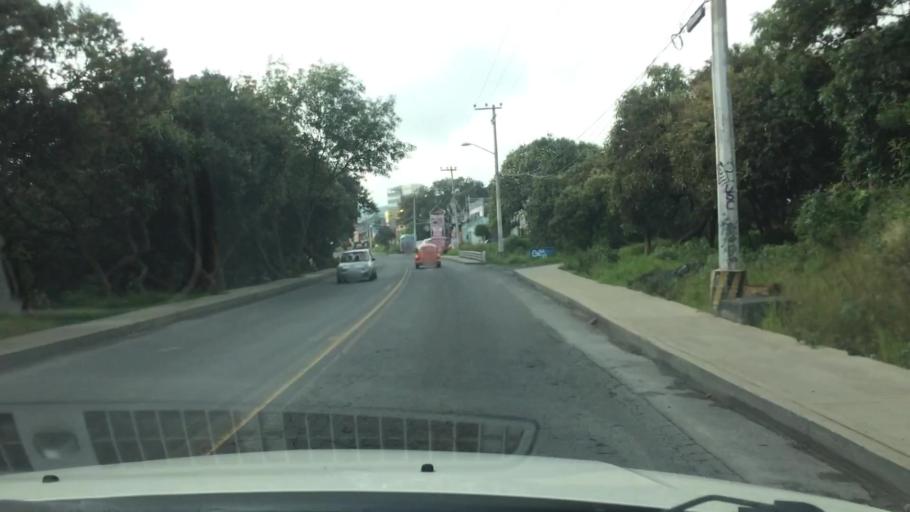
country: MX
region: Mexico City
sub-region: Tlalpan
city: Lomas de Tepemecatl
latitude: 19.2699
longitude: -99.2057
